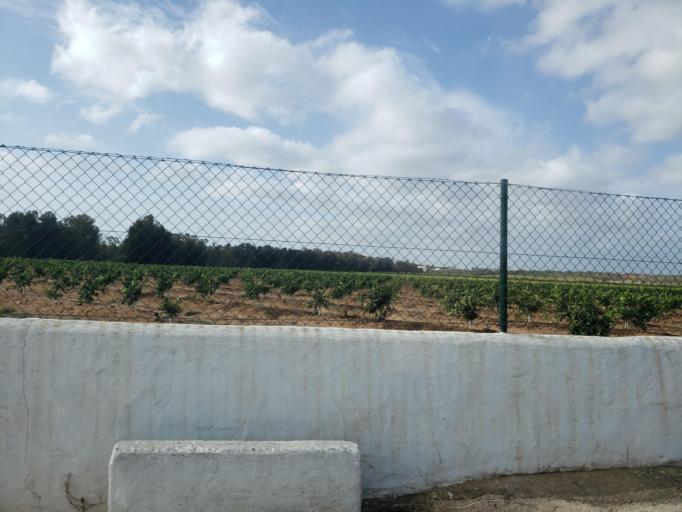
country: PT
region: Faro
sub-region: Portimao
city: Alvor
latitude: 37.1675
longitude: -8.5782
